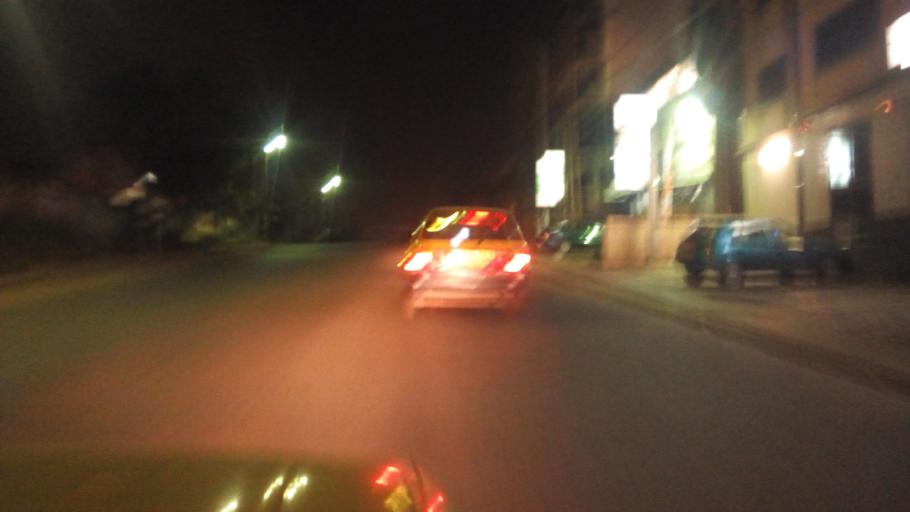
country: CM
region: Centre
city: Yaounde
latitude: 3.8388
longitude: 11.4872
